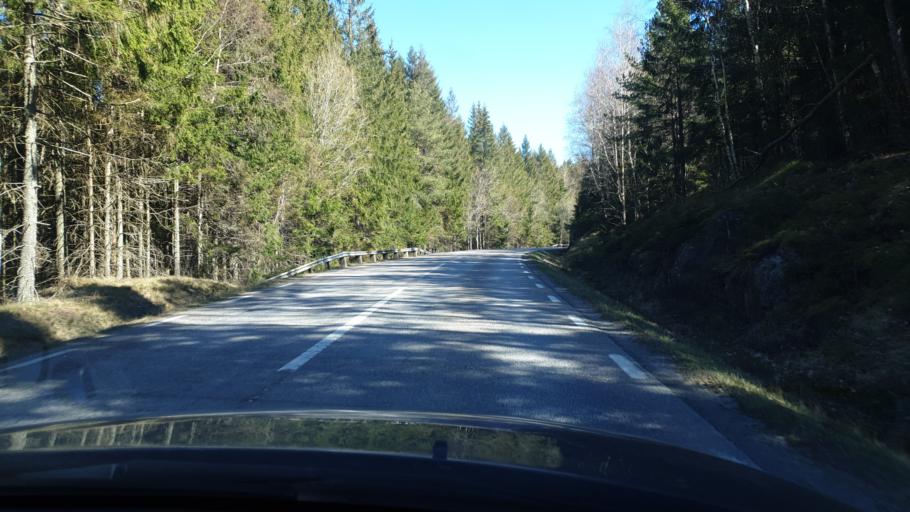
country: SE
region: Vaestra Goetaland
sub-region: Tanums Kommun
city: Tanumshede
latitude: 58.7437
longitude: 11.4918
